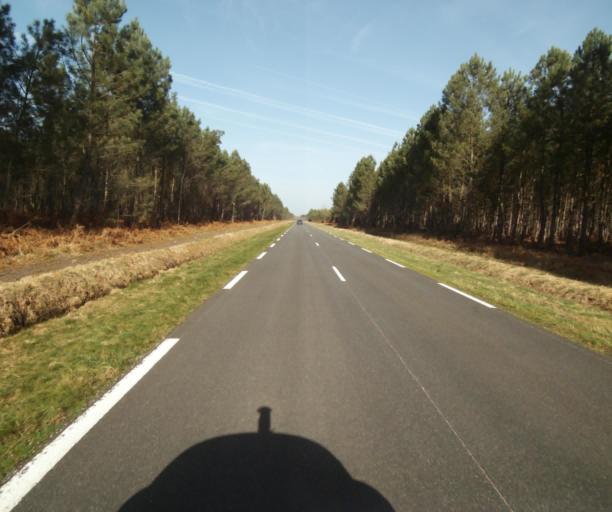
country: FR
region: Aquitaine
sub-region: Departement de la Gironde
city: Grignols
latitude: 44.1841
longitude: -0.0887
